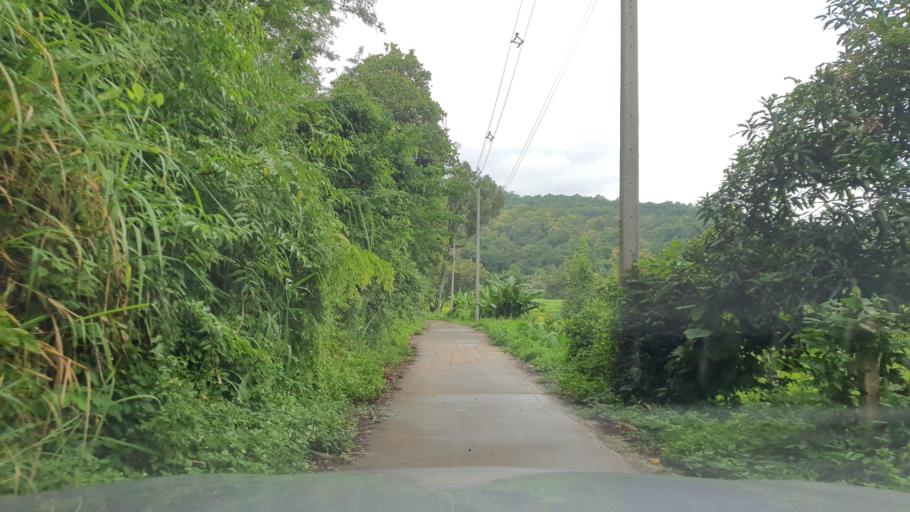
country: TH
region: Chiang Mai
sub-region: Amphoe Chiang Dao
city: Chiang Dao
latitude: 19.3355
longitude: 98.9278
